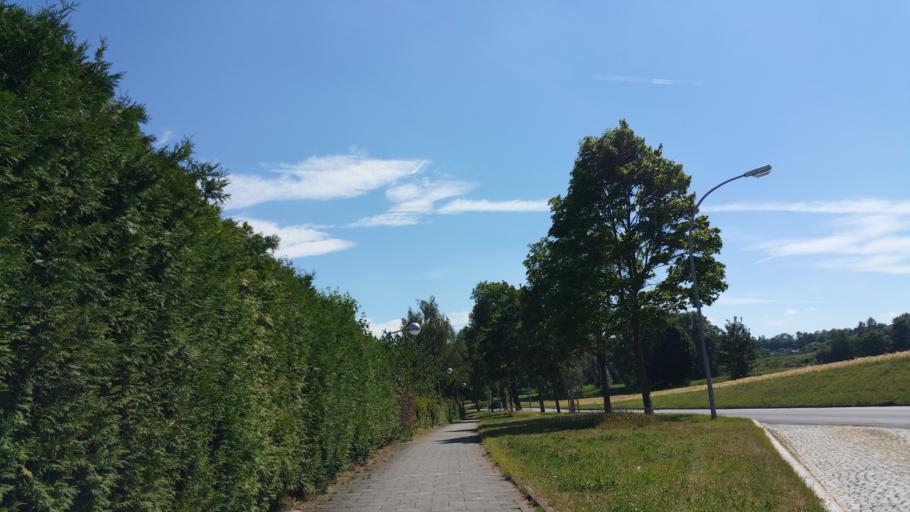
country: DE
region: Bavaria
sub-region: Upper Franconia
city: Hof
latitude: 50.3331
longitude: 11.8937
